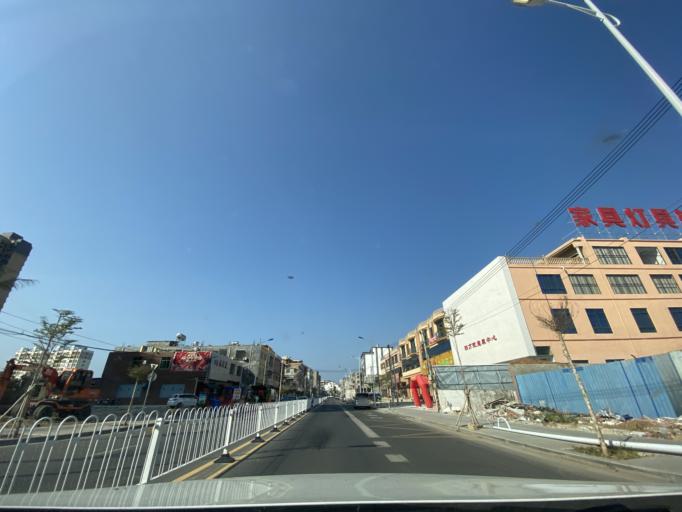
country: CN
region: Hainan
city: Yingzhou
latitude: 18.4168
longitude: 109.8538
